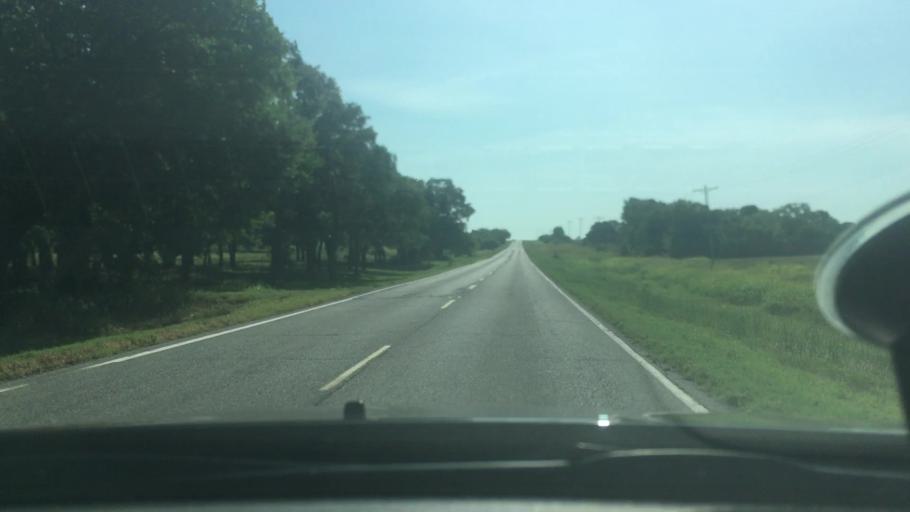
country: US
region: Oklahoma
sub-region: Garvin County
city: Pauls Valley
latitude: 34.6519
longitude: -97.2916
